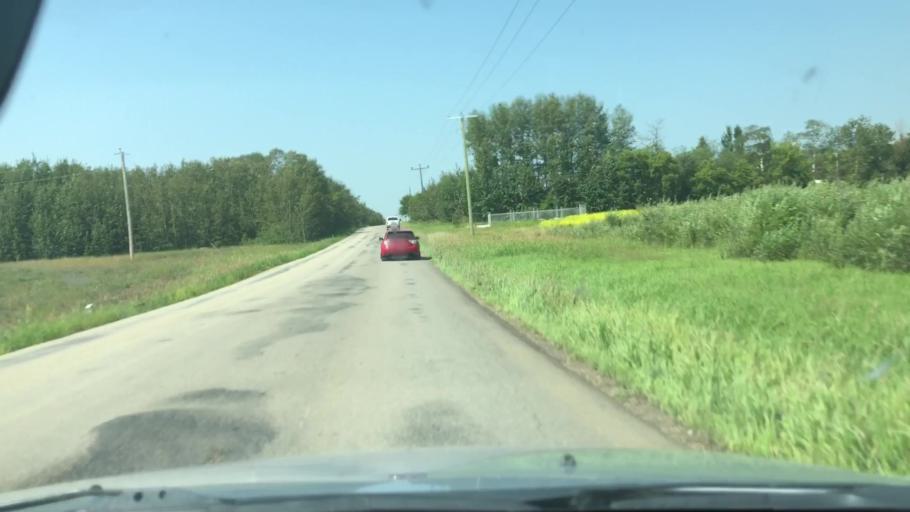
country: CA
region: Alberta
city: Devon
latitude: 53.5122
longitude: -113.7240
